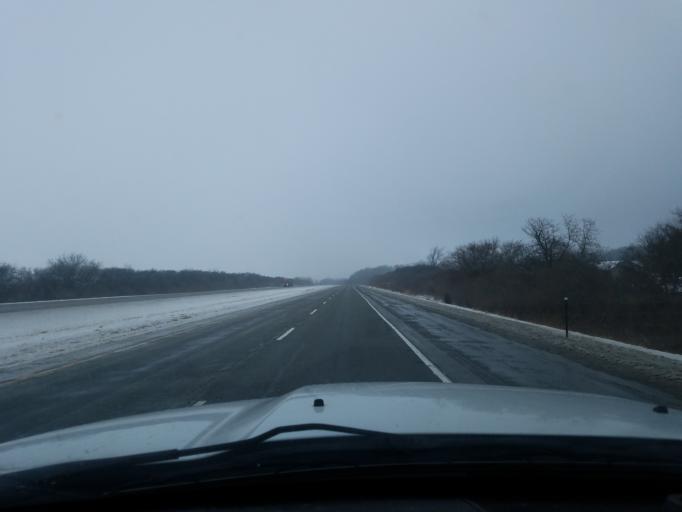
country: US
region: Indiana
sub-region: Fulton County
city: Rochester
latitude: 41.0353
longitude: -86.1901
